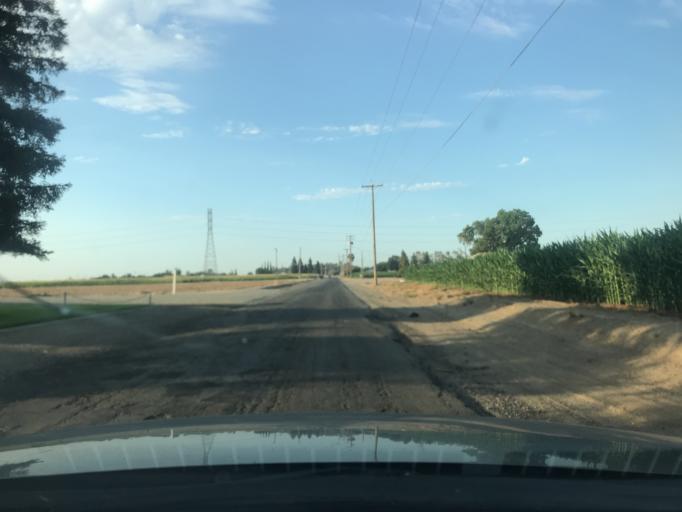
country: US
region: California
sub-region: Merced County
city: Atwater
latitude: 37.3517
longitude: -120.5496
